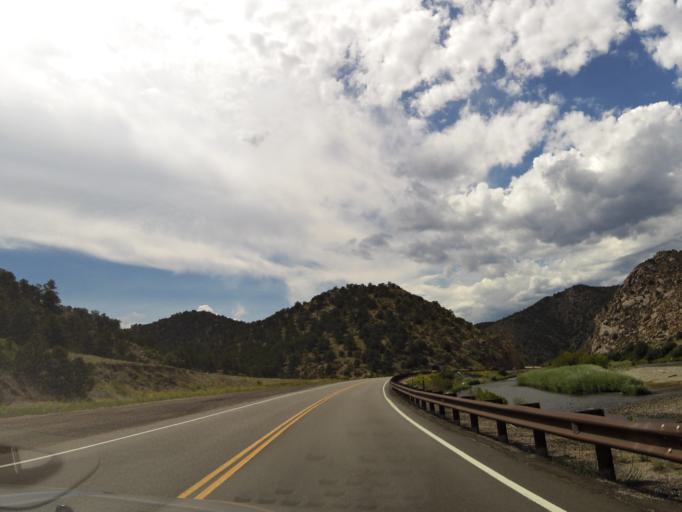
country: US
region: Colorado
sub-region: Custer County
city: Westcliffe
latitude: 38.3906
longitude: -105.6431
